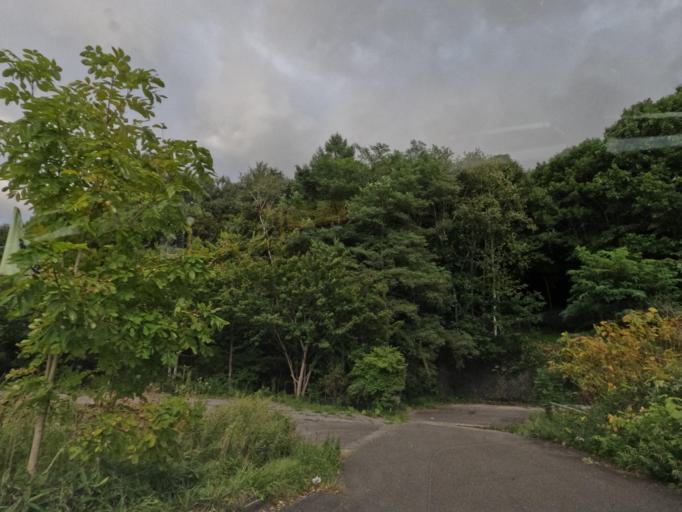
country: JP
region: Hokkaido
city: Muroran
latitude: 42.3762
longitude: 140.9612
